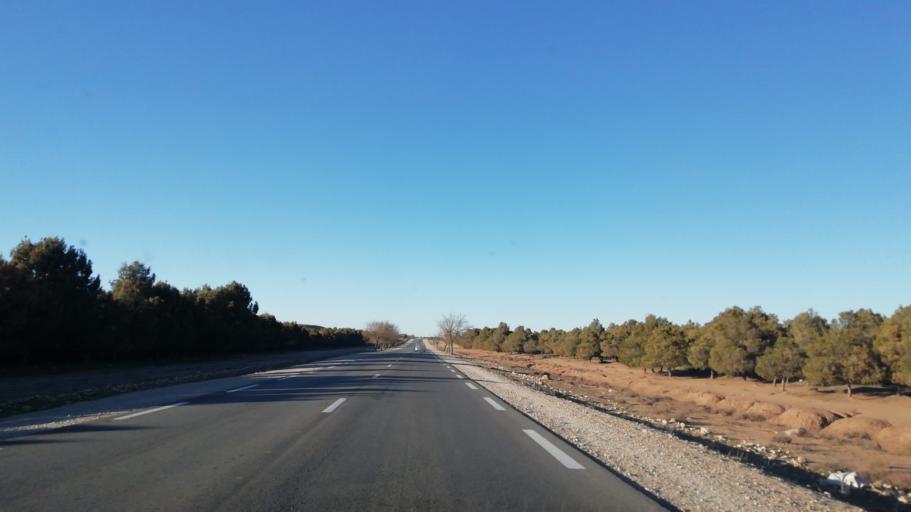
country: DZ
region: Tlemcen
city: Sebdou
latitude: 34.5116
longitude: -1.2835
